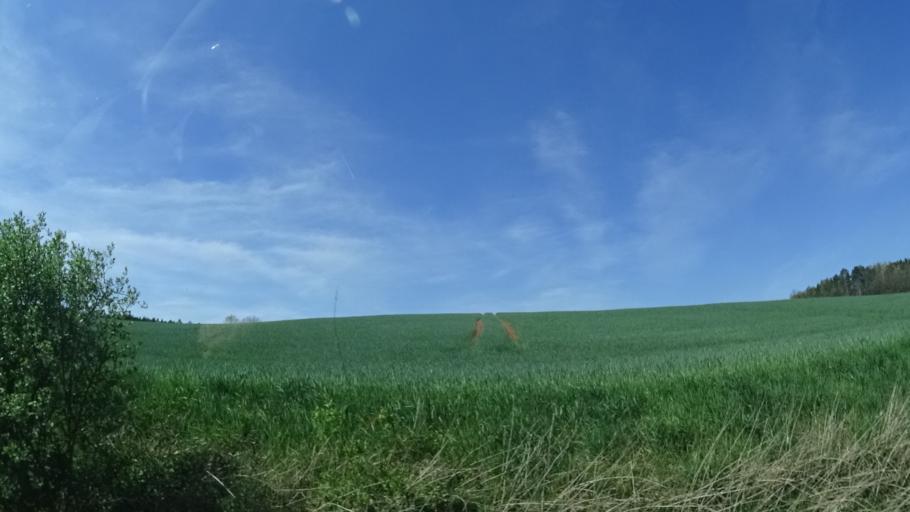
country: DE
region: Bavaria
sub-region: Upper Franconia
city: Weitramsdorf
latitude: 50.2882
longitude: 10.7875
